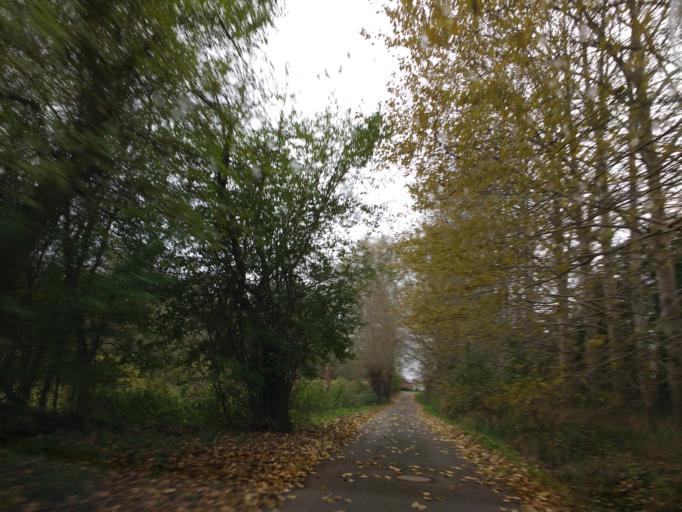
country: DE
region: Mecklenburg-Vorpommern
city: Ostseebad Boltenhagen
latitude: 53.9817
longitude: 11.1998
